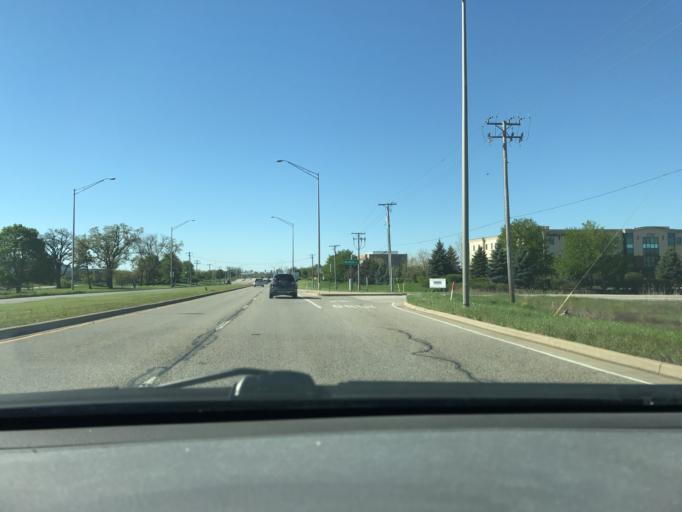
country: US
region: Illinois
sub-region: Kane County
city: Sleepy Hollow
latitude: 42.0786
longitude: -88.3356
